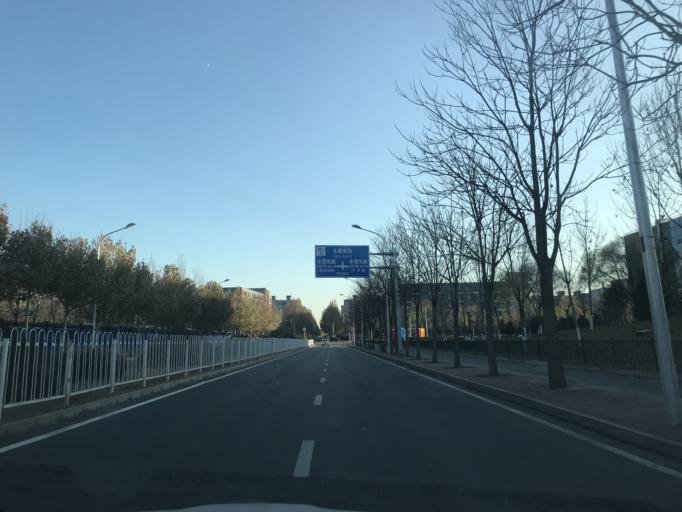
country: CN
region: Beijing
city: Xibeiwang
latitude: 40.0693
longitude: 116.2468
